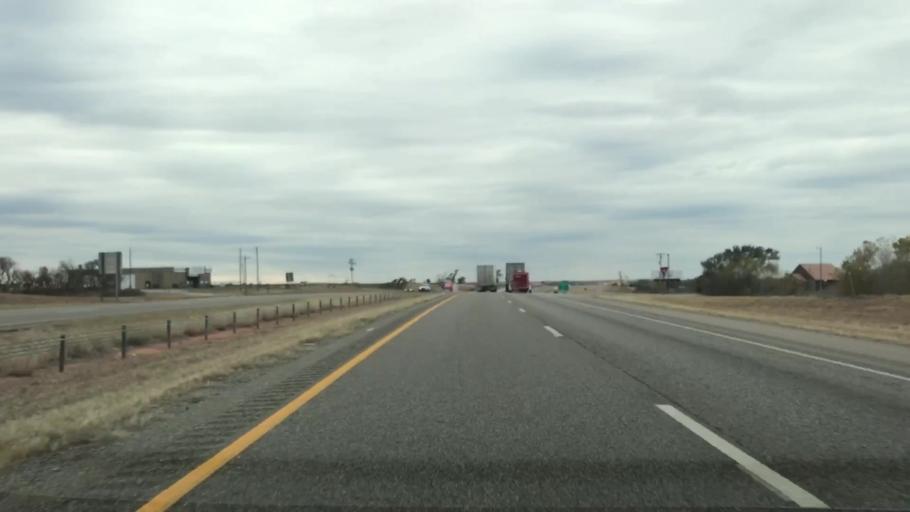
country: US
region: Oklahoma
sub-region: Custer County
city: Clinton
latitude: 35.4805
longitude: -99.0265
